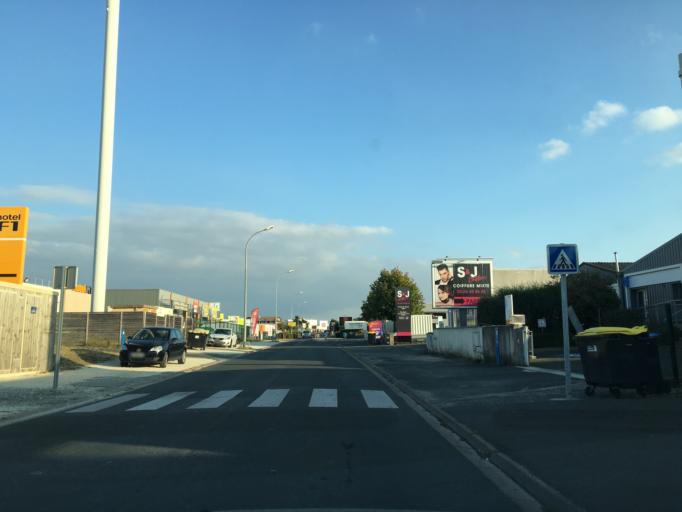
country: FR
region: Poitou-Charentes
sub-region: Departement de la Charente-Maritime
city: Angoulins
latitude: 46.1086
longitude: -1.1008
